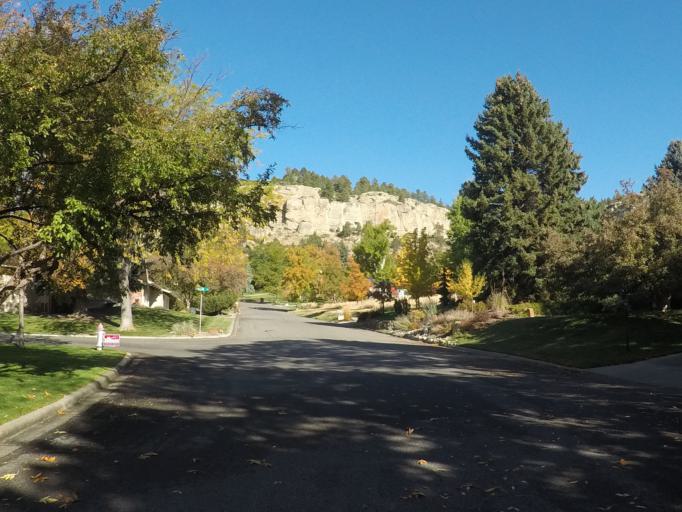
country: US
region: Montana
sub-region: Yellowstone County
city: Billings
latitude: 45.7999
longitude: -108.5831
